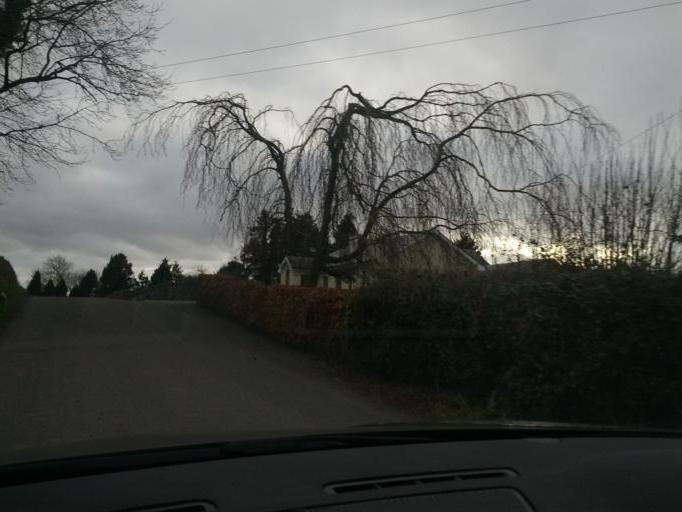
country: IE
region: Leinster
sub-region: An Iarmhi
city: Moate
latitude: 53.3839
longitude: -7.8246
